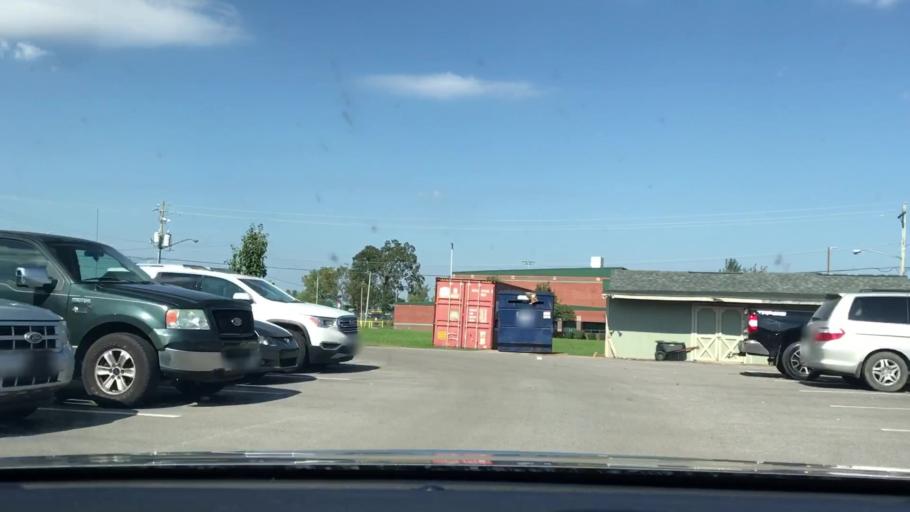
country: US
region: Kentucky
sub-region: Warren County
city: Plano
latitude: 36.9251
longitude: -86.4127
